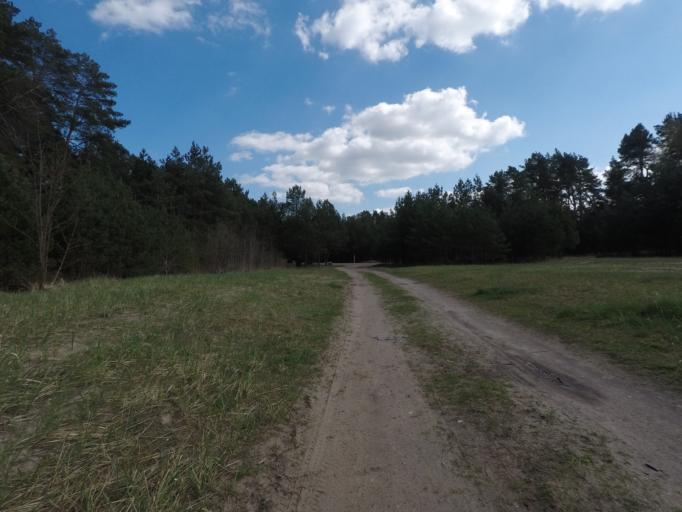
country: DE
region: Brandenburg
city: Melchow
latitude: 52.8317
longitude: 13.7145
